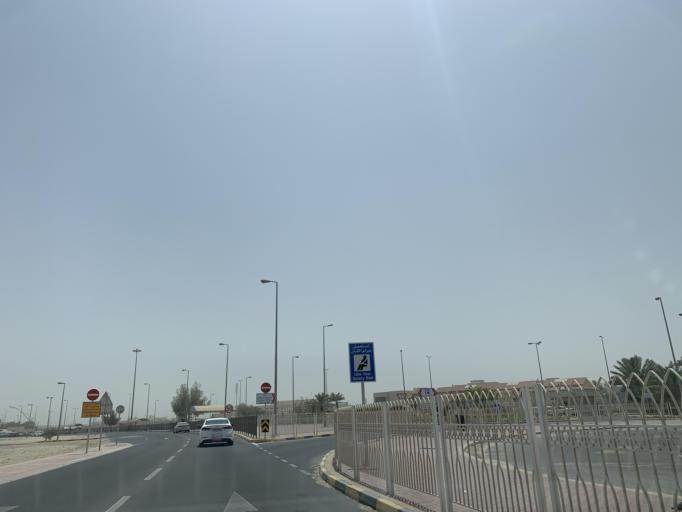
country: BH
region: Northern
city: Madinat `Isa
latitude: 26.1596
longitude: 50.5312
